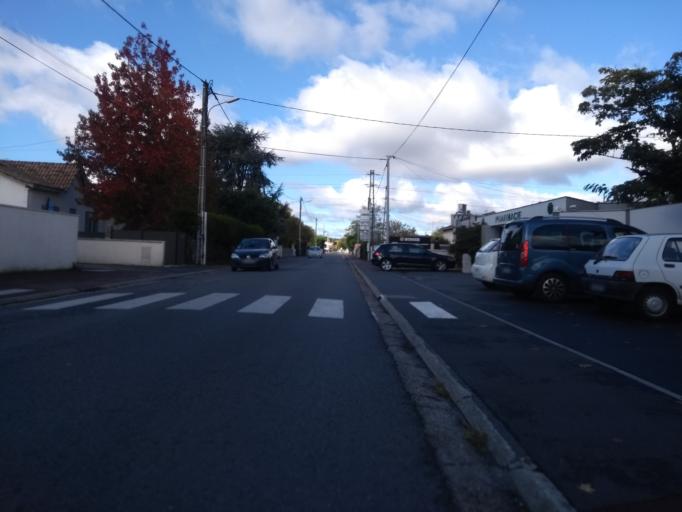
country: FR
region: Aquitaine
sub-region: Departement de la Gironde
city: Saint-Aubin-de-Medoc
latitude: 44.7689
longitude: -0.6973
